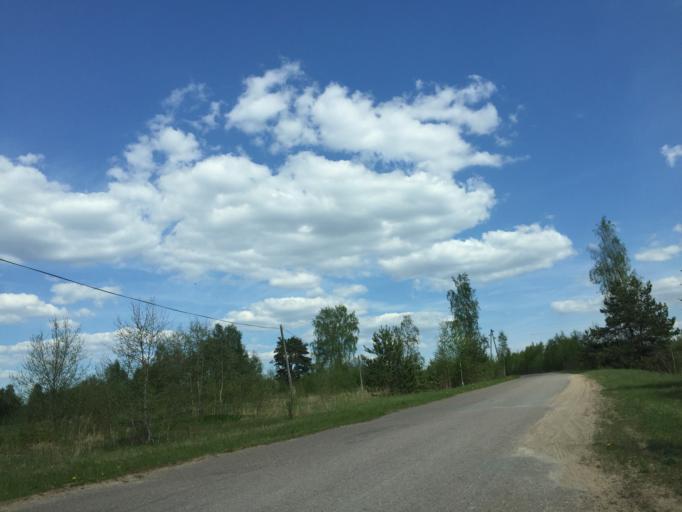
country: LV
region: Limbazu Rajons
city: Limbazi
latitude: 57.4195
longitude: 24.6864
